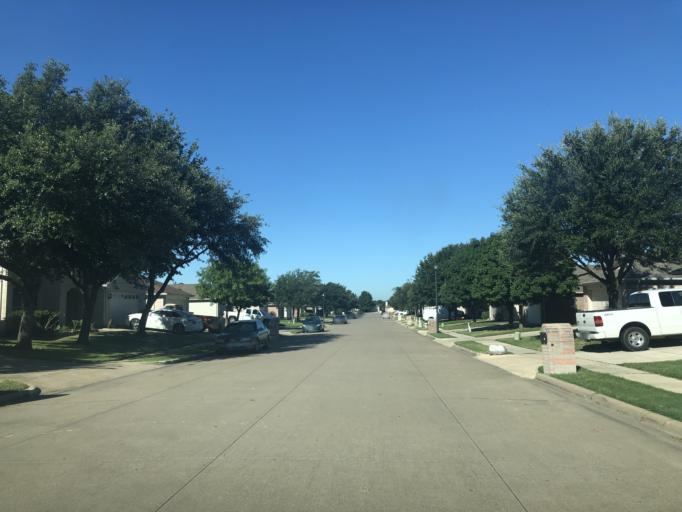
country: US
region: Texas
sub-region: Dallas County
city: Duncanville
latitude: 32.6575
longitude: -96.9746
